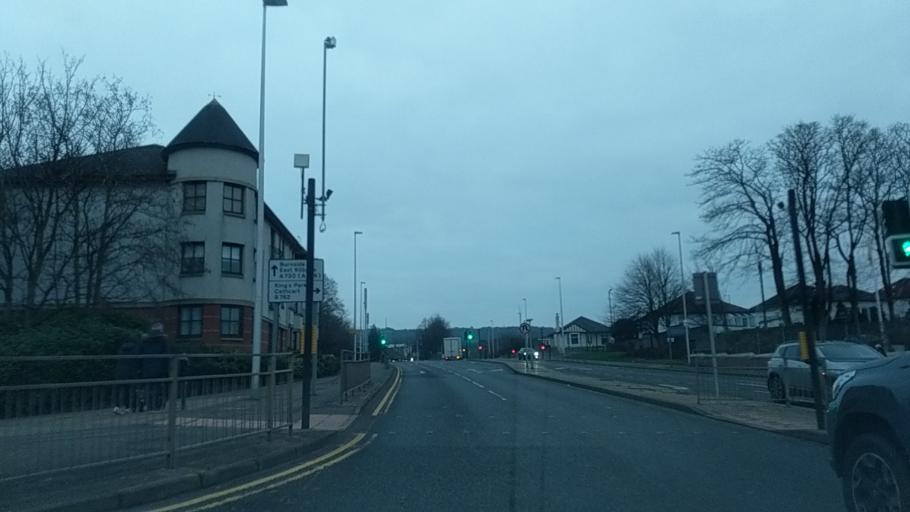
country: GB
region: Scotland
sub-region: South Lanarkshire
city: Rutherglen
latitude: 55.8204
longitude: -4.2155
